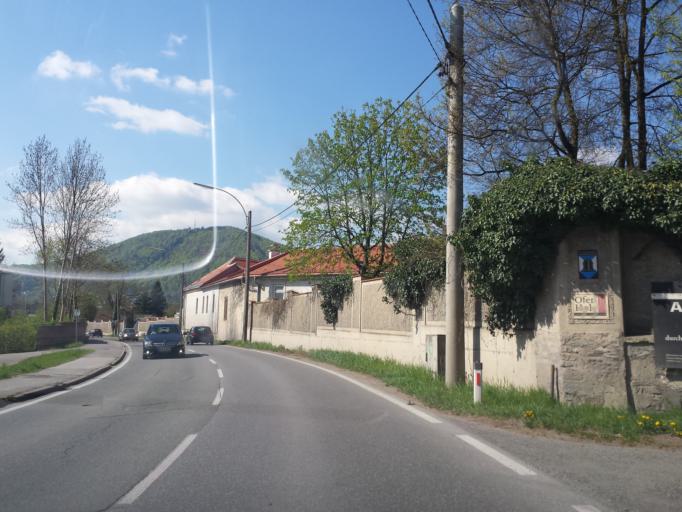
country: AT
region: Styria
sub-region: Graz Stadt
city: Goesting
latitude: 47.1114
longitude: 15.4035
